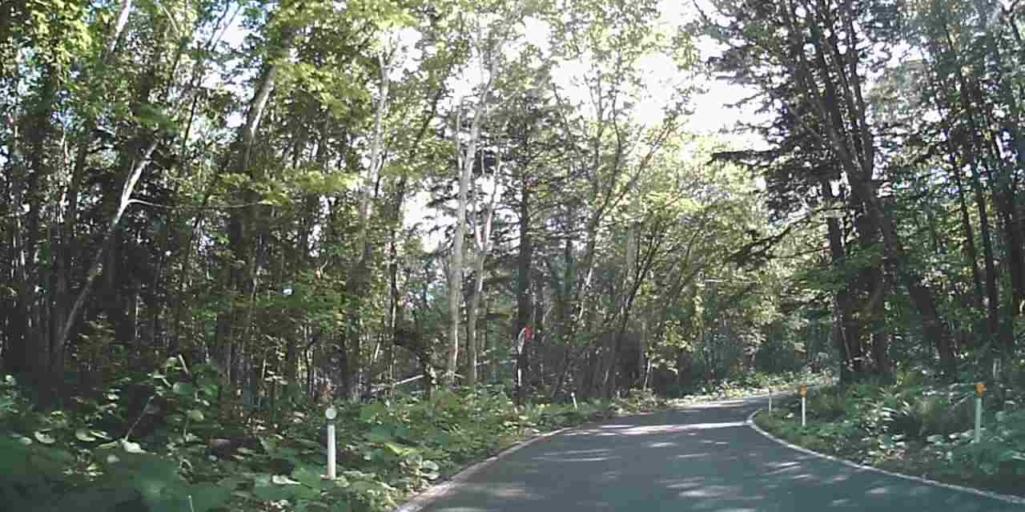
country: JP
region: Hokkaido
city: Shiraoi
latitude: 42.7192
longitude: 141.4103
